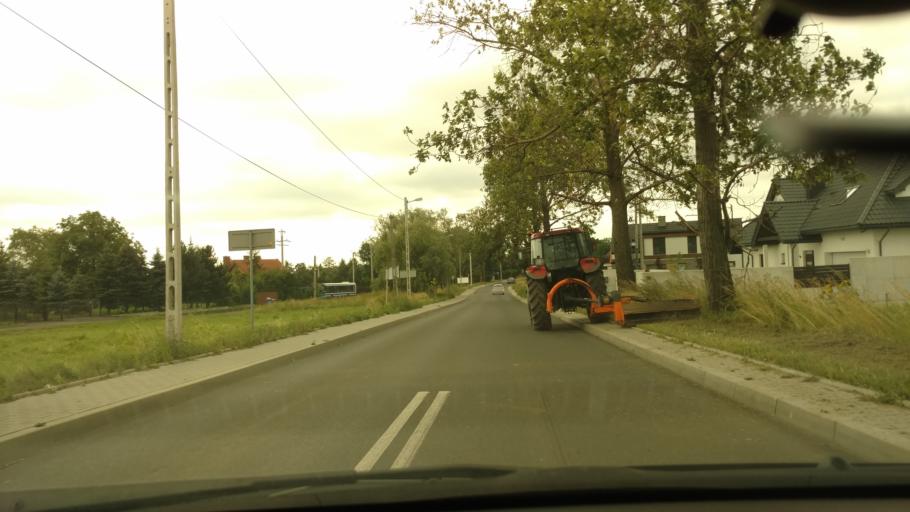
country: PL
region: Lesser Poland Voivodeship
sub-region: Powiat krakowski
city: Zielonki
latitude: 50.1246
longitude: 19.9389
